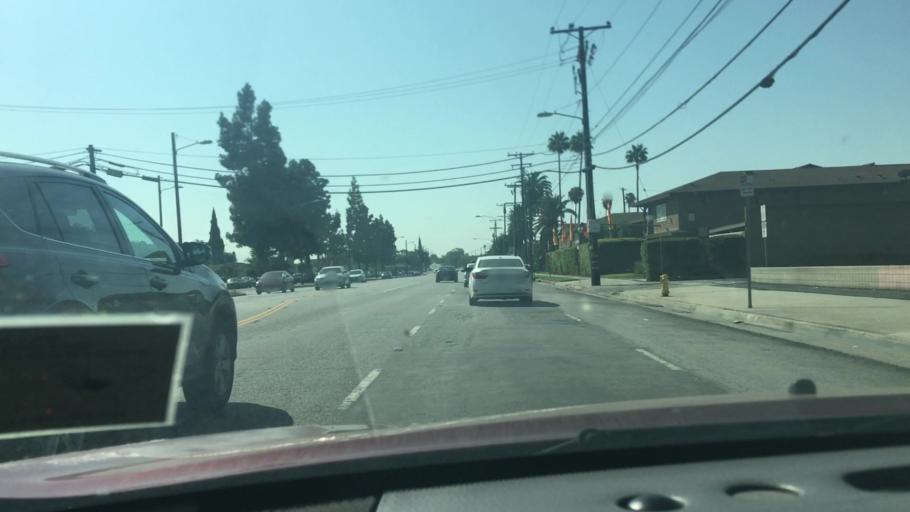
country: US
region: California
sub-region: Los Angeles County
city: South Whittier
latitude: 33.9423
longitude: -118.0270
